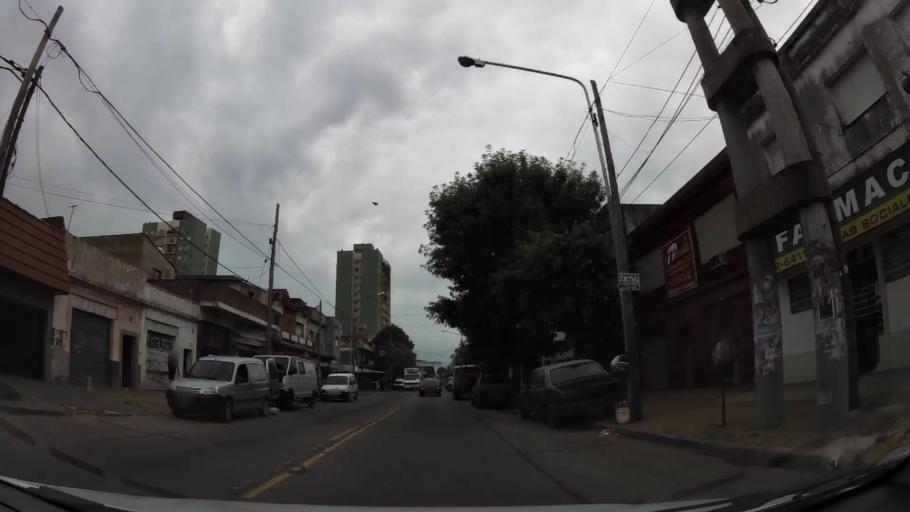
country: AR
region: Buenos Aires
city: San Justo
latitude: -34.6730
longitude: -58.5291
